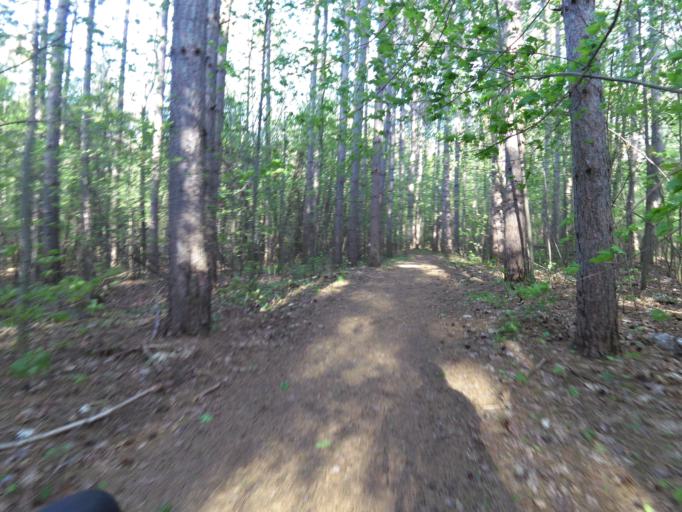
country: CA
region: Ontario
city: Ottawa
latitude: 45.3267
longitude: -75.7342
